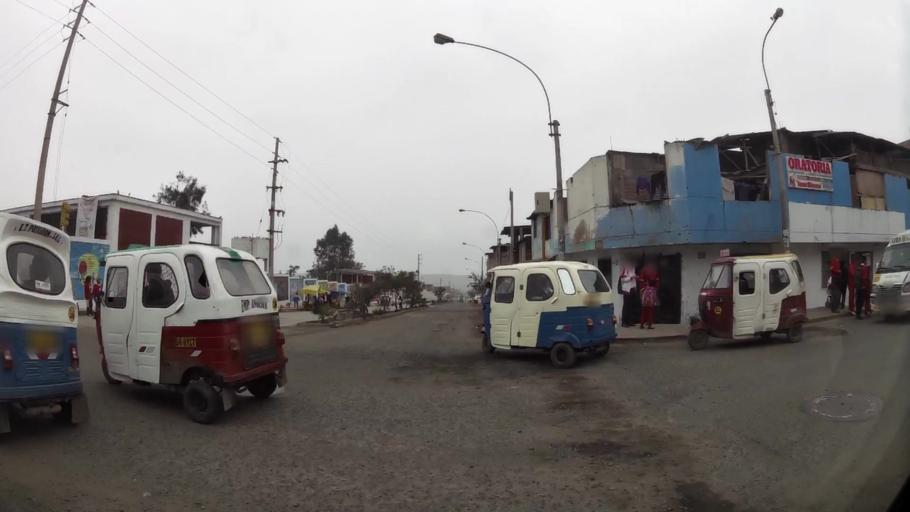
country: PE
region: Lima
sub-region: Lima
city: Surco
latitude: -12.2182
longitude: -76.9338
